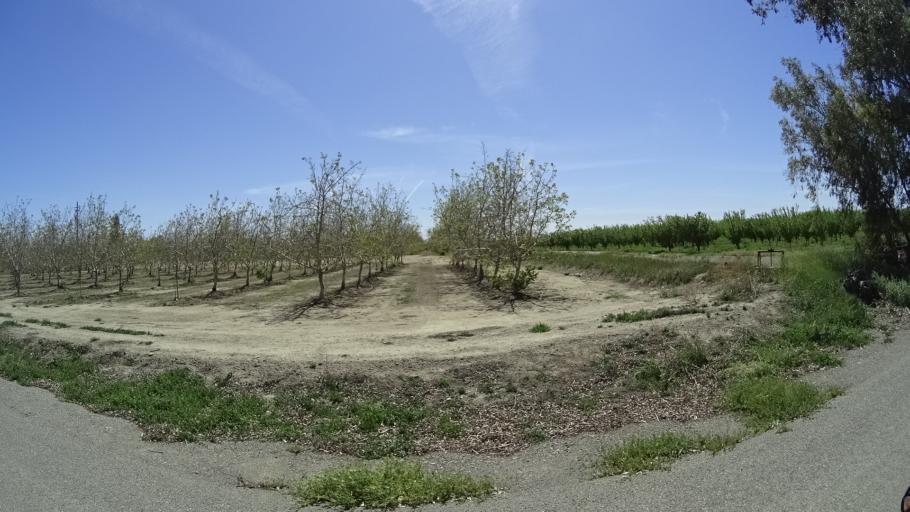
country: US
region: California
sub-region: Glenn County
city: Orland
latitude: 39.7322
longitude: -122.1087
